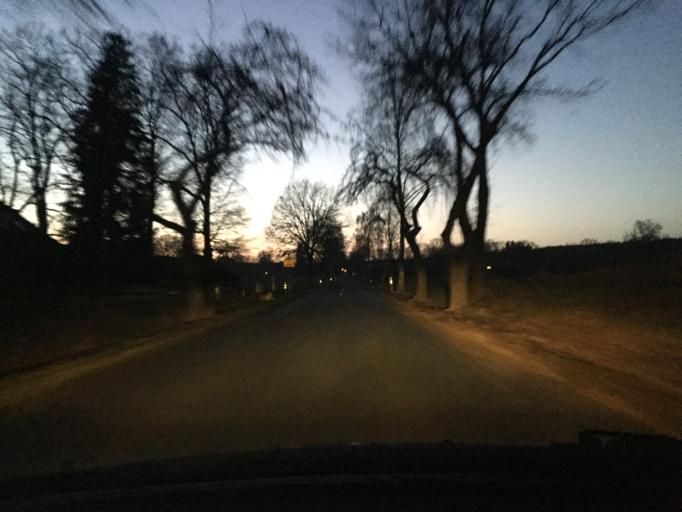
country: DE
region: Lower Saxony
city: Gohrde
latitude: 53.1660
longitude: 10.8597
